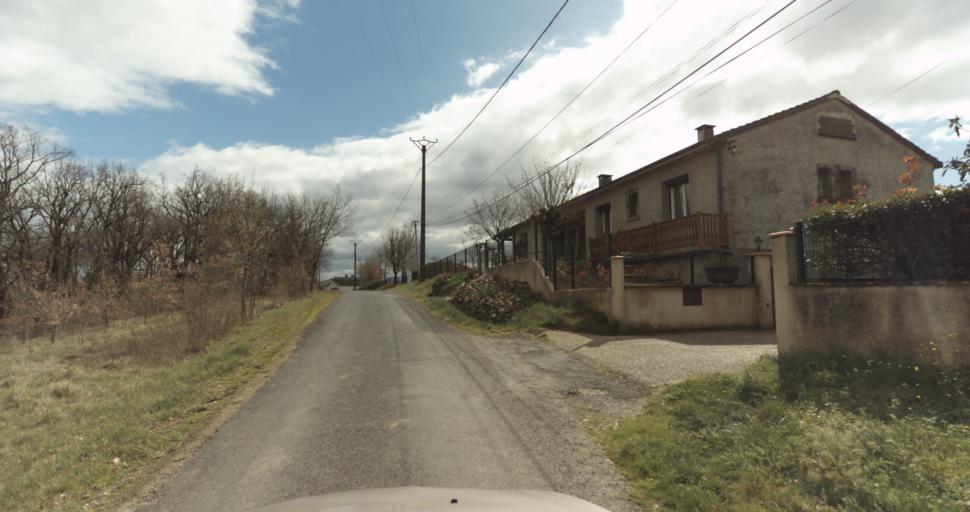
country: FR
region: Midi-Pyrenees
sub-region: Departement du Tarn
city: Puygouzon
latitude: 43.8835
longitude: 2.1509
